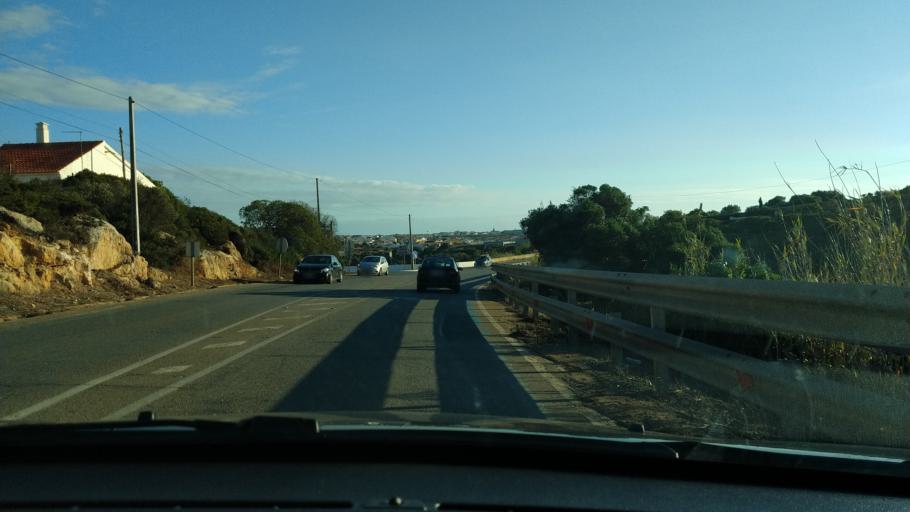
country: PT
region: Faro
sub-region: Vila do Bispo
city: Sagres
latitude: 37.0232
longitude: -8.9378
